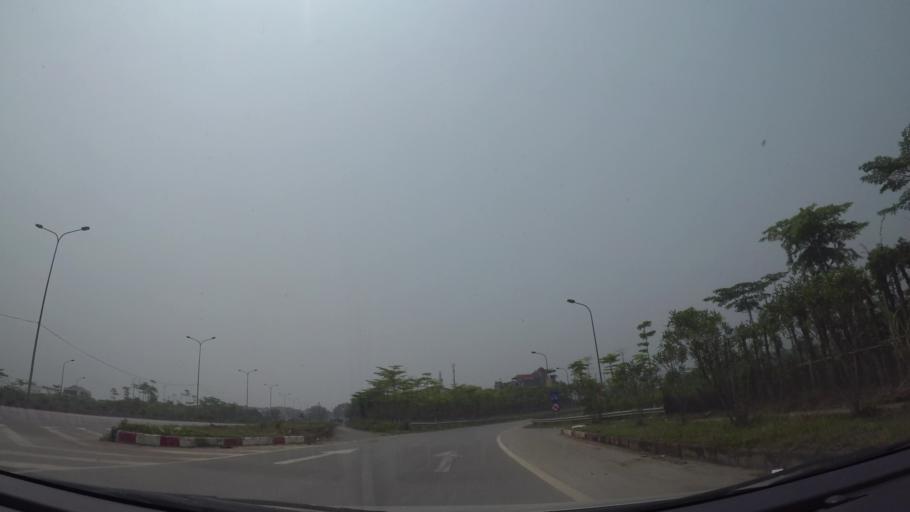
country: VN
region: Ha Noi
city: Lien Quan
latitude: 20.9888
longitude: 105.5251
